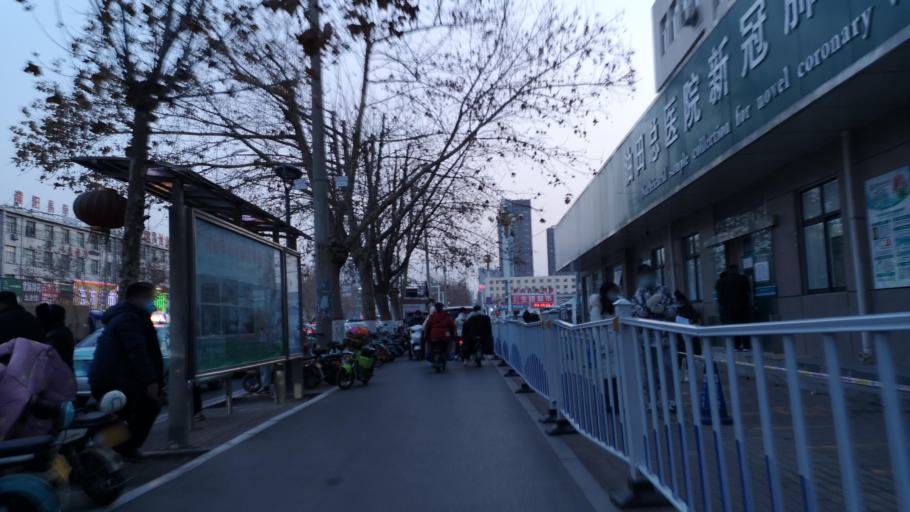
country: CN
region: Henan Sheng
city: Zhongyuanlu
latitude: 35.7716
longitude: 115.0695
